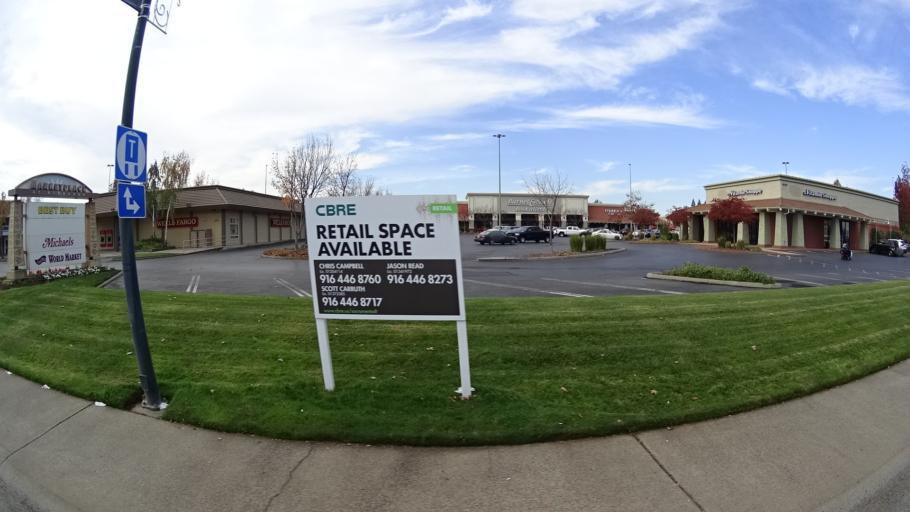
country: US
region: California
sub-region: Sacramento County
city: Fair Oaks
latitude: 38.6747
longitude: -121.2717
